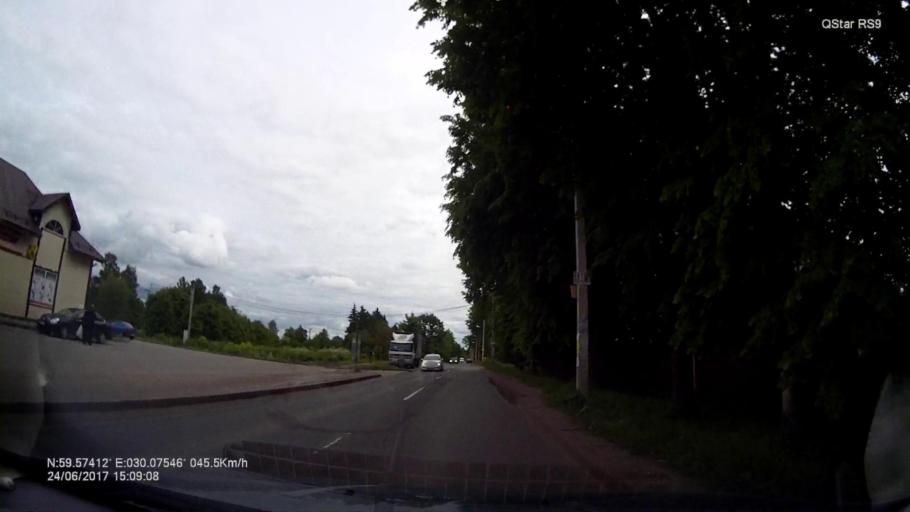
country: RU
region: Leningrad
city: Mariyenburg
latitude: 59.5740
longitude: 30.0757
